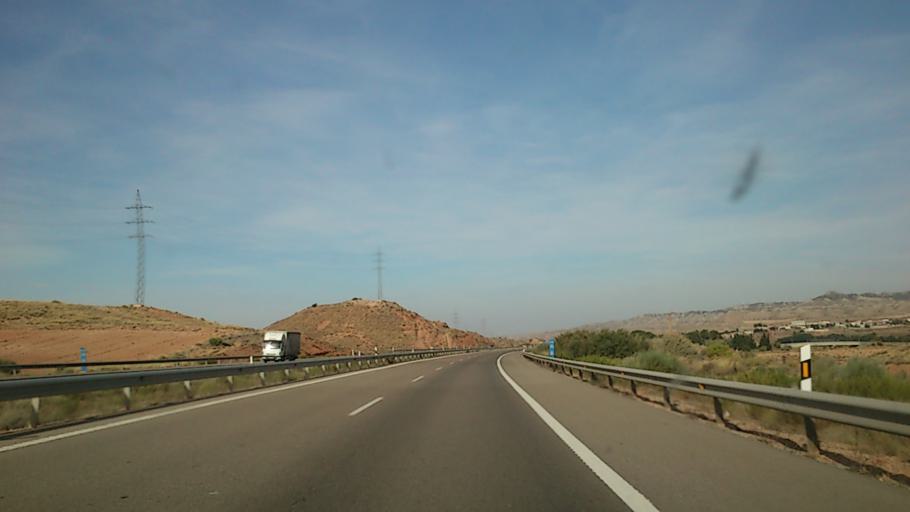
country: ES
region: Aragon
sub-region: Provincia de Zaragoza
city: Mozota
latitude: 41.5001
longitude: -1.0596
